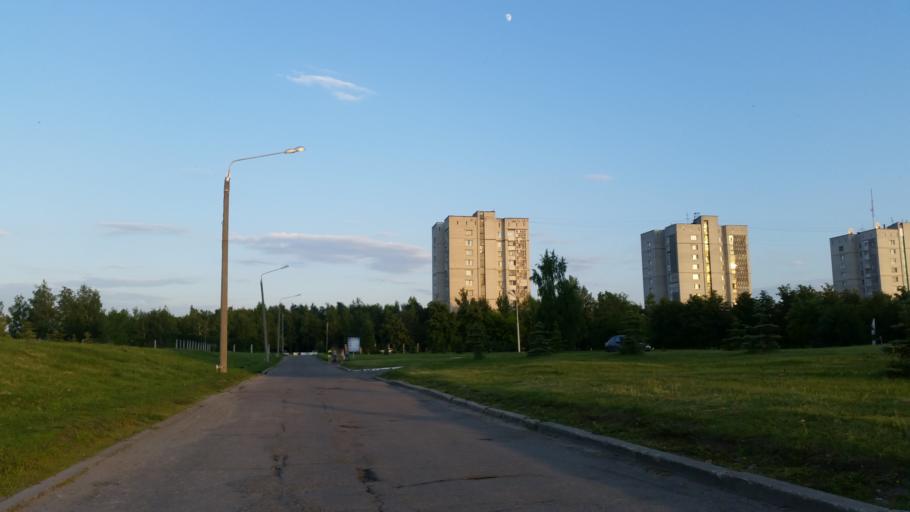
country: RU
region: Ulyanovsk
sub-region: Ulyanovskiy Rayon
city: Ulyanovsk
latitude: 54.3514
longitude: 48.3911
